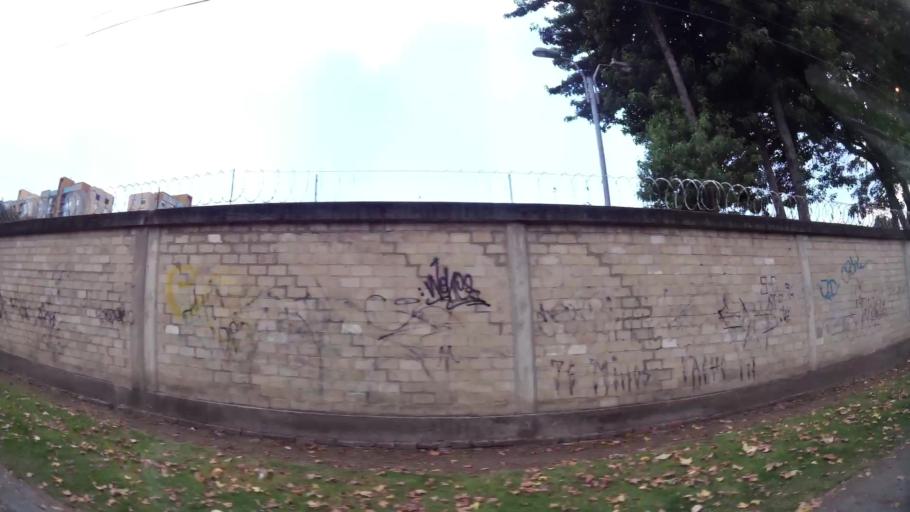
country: CO
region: Cundinamarca
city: La Calera
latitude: 4.7432
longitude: -74.0283
